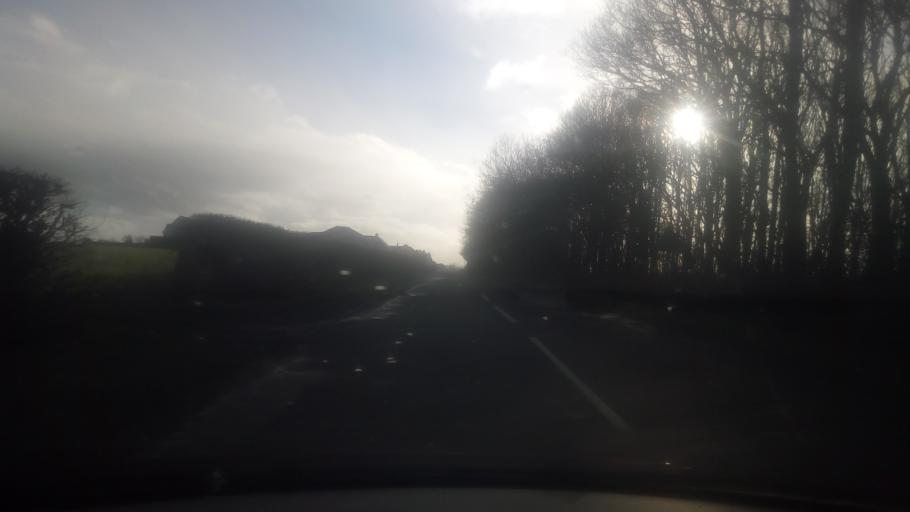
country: GB
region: Scotland
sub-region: The Scottish Borders
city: Kelso
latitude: 55.6401
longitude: -2.4064
